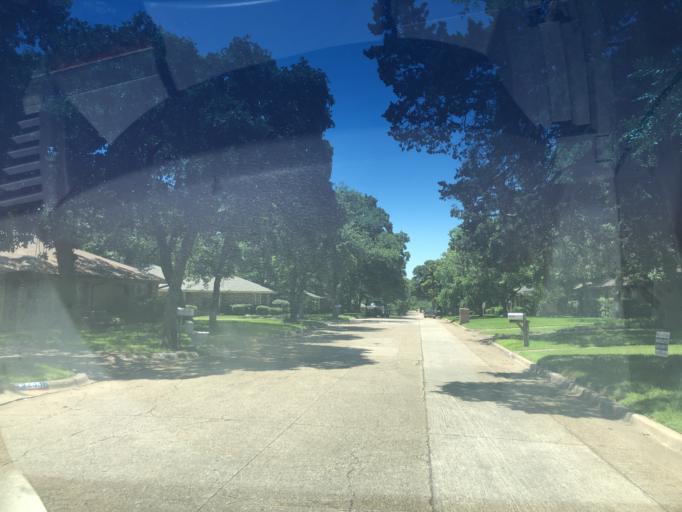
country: US
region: Texas
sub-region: Dallas County
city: Grand Prairie
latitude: 32.7783
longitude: -97.0357
